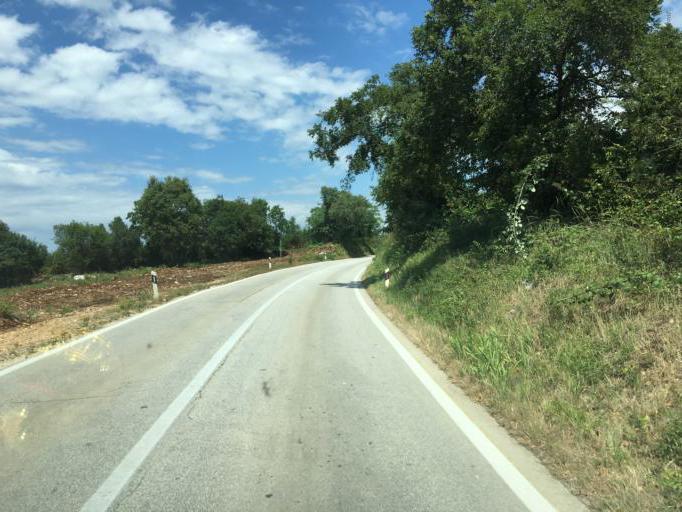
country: HR
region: Istarska
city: Vrsar
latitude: 45.1745
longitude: 13.7417
